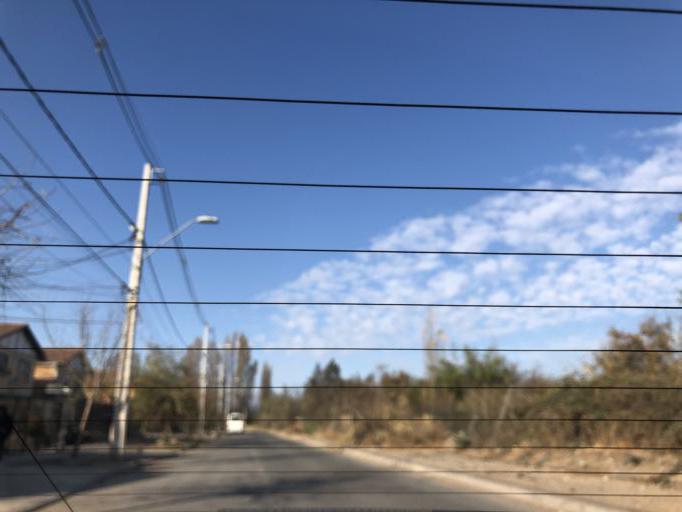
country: CL
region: Santiago Metropolitan
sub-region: Provincia de Cordillera
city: Puente Alto
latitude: -33.6322
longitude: -70.5956
